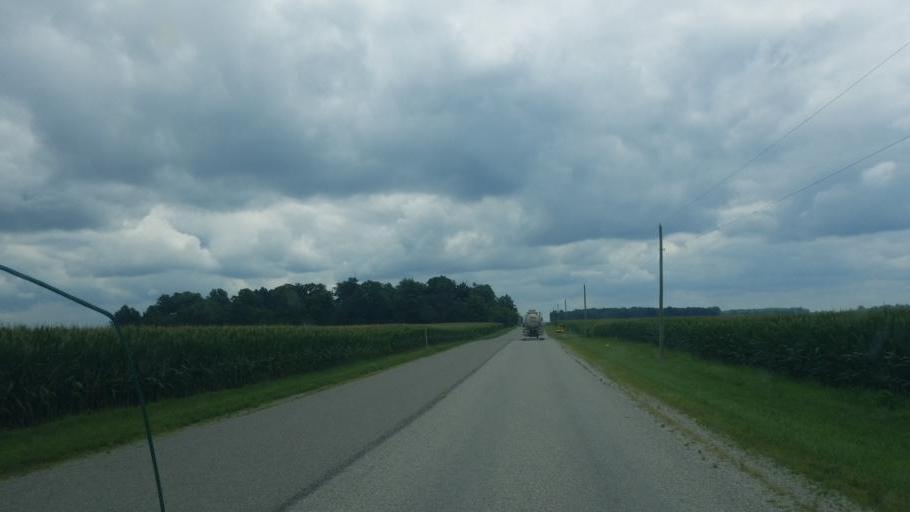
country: US
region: Indiana
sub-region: Wells County
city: Bluffton
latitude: 40.6552
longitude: -85.1345
